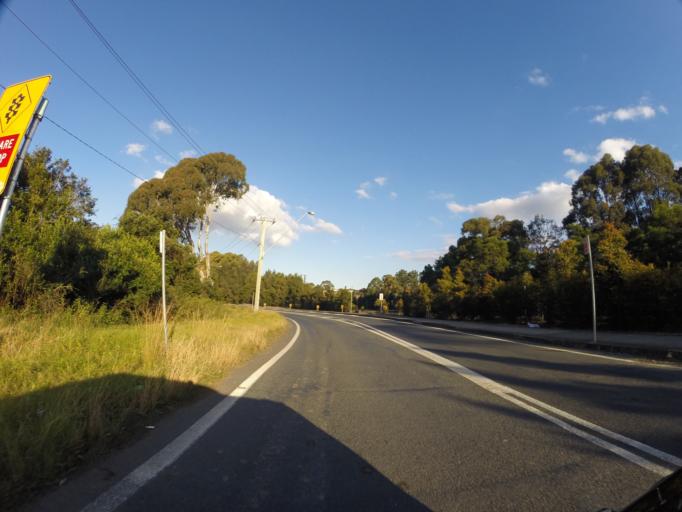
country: AU
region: New South Wales
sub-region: Wollongong
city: Cordeaux Heights
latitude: -34.4435
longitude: 150.8425
